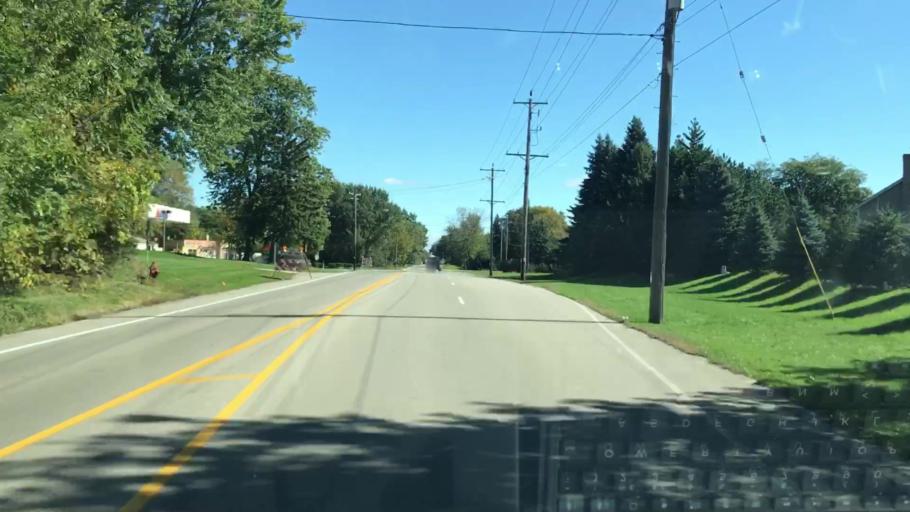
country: US
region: Wisconsin
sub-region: Waukesha County
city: Lannon
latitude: 43.1046
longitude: -88.1370
